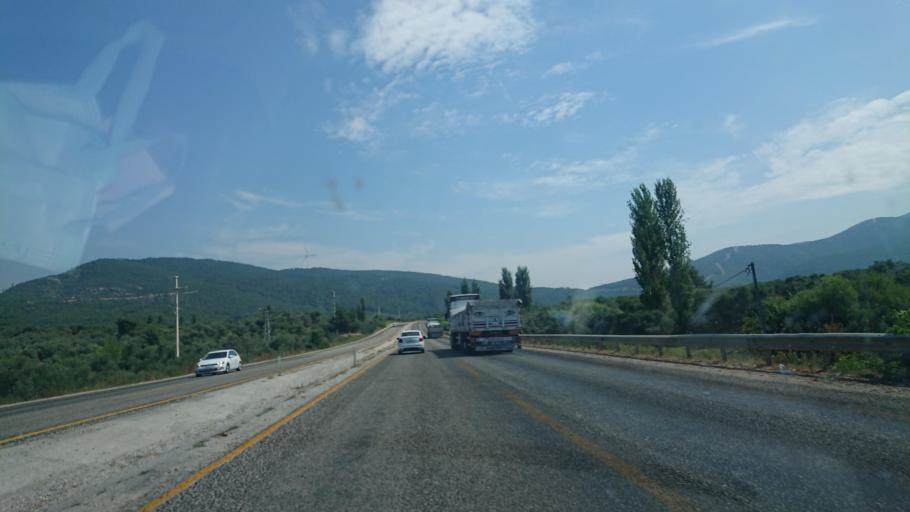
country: TR
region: Izmir
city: Dagkizilca
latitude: 38.3302
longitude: 27.4182
